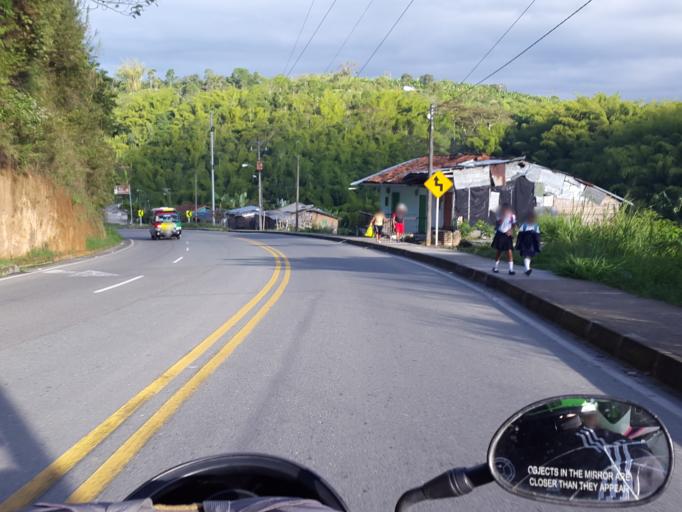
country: CO
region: Quindio
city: Montenegro
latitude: 4.5683
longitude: -75.7540
